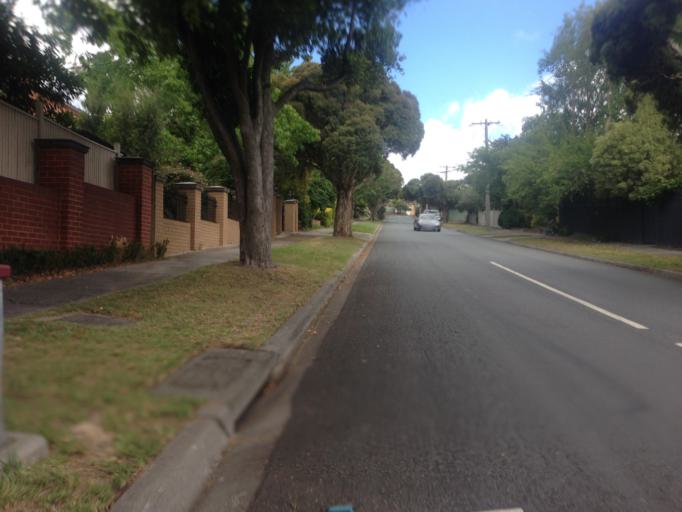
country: AU
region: Victoria
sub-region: Boroondara
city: Balwyn North
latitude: -37.7864
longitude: 145.0848
